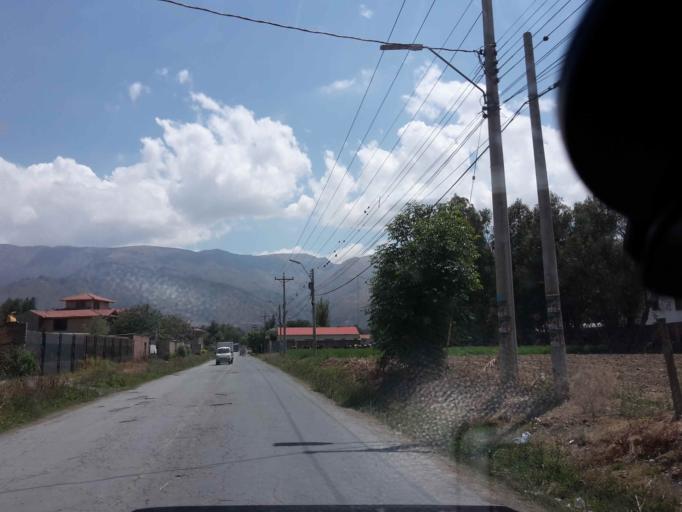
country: BO
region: Cochabamba
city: Cochabamba
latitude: -17.3546
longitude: -66.2268
